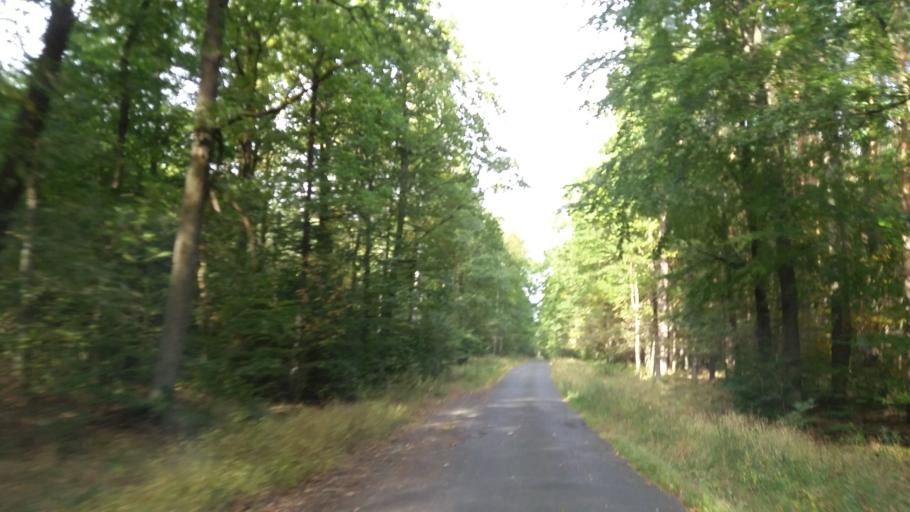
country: PL
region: West Pomeranian Voivodeship
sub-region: Powiat choszczenski
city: Krzecin
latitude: 52.9804
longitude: 15.4609
